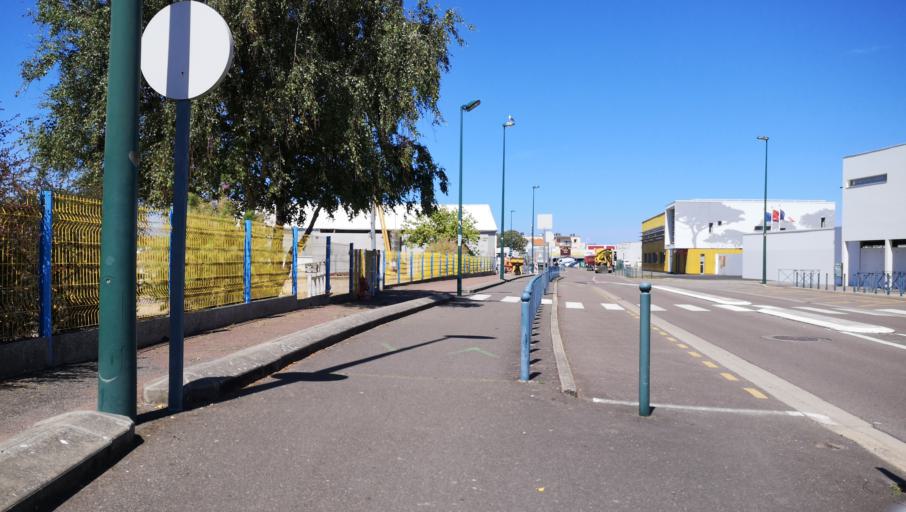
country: FR
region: Pays de la Loire
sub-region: Departement de la Vendee
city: Les Sables-d'Olonne
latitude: 46.5118
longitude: -1.7740
